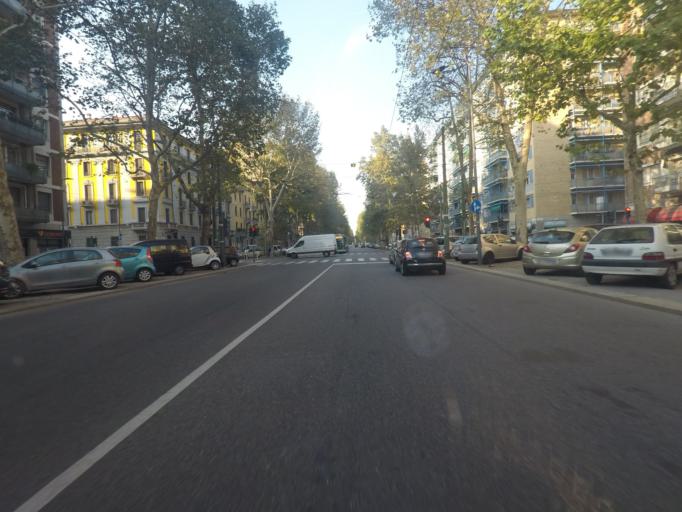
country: IT
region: Lombardy
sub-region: Citta metropolitana di Milano
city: Milano
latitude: 45.4651
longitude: 9.2240
